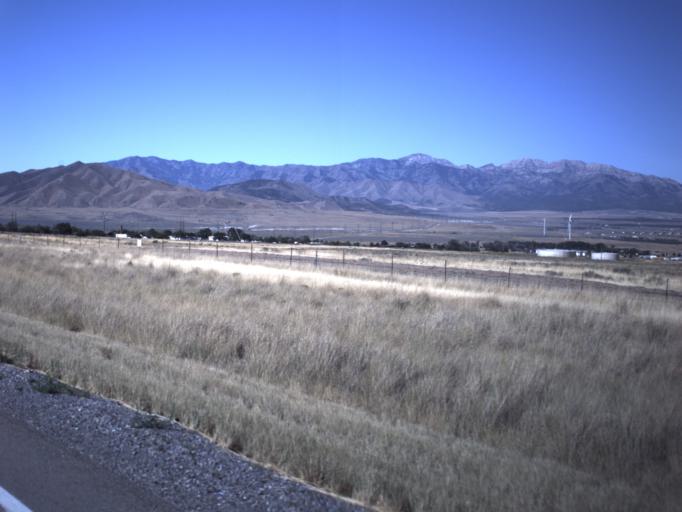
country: US
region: Utah
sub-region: Tooele County
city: Tooele
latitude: 40.5027
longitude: -112.3223
